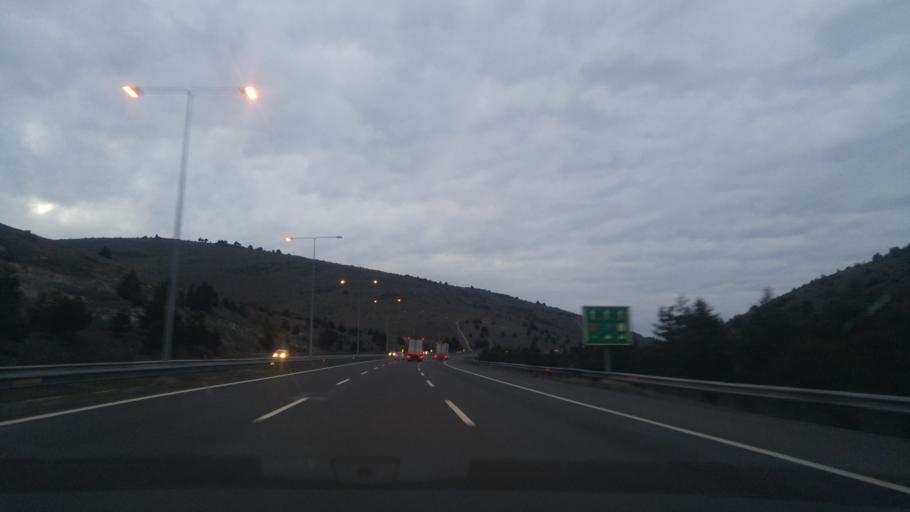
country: TR
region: Ankara
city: Pecenek
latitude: 40.5270
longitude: 32.2871
